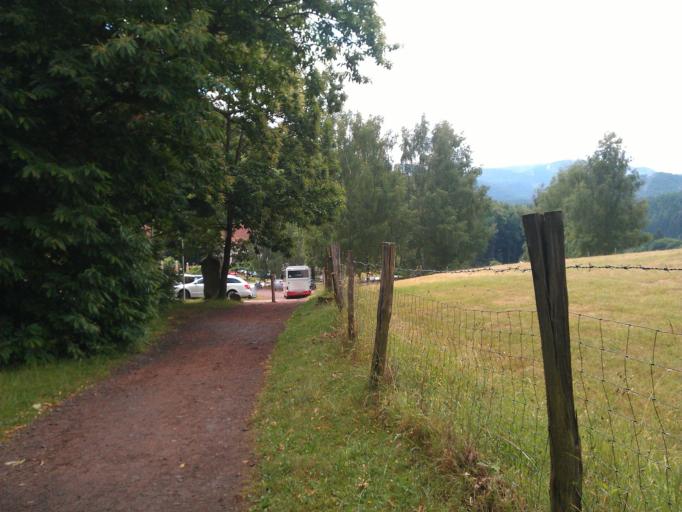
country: DE
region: Rheinland-Pfalz
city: Nothweiler
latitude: 49.0480
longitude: 7.7877
